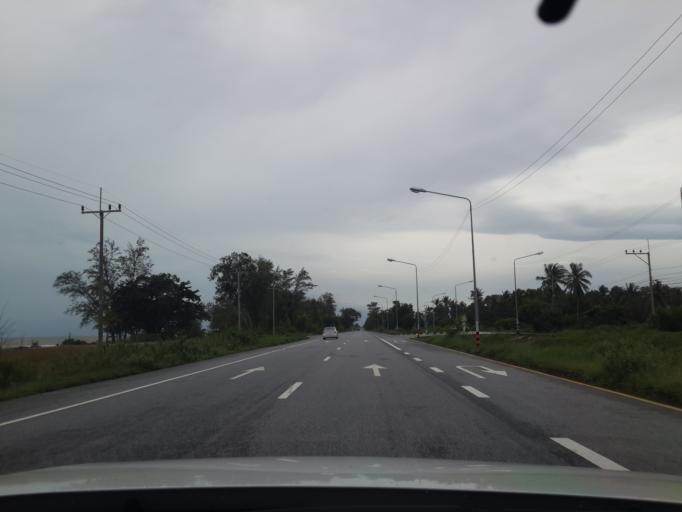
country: TH
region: Songkhla
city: Chana
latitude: 6.9433
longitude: 100.8679
